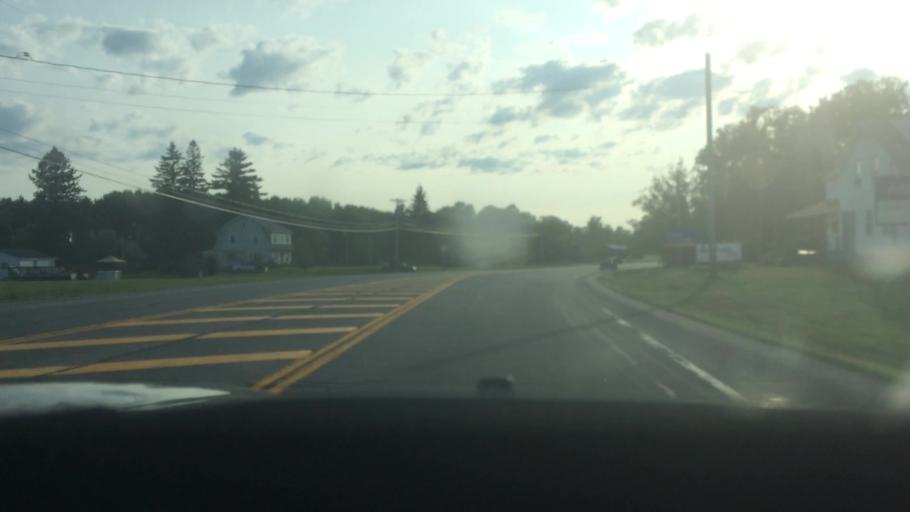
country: US
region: New York
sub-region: St. Lawrence County
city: Ogdensburg
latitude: 44.6724
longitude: -75.4221
